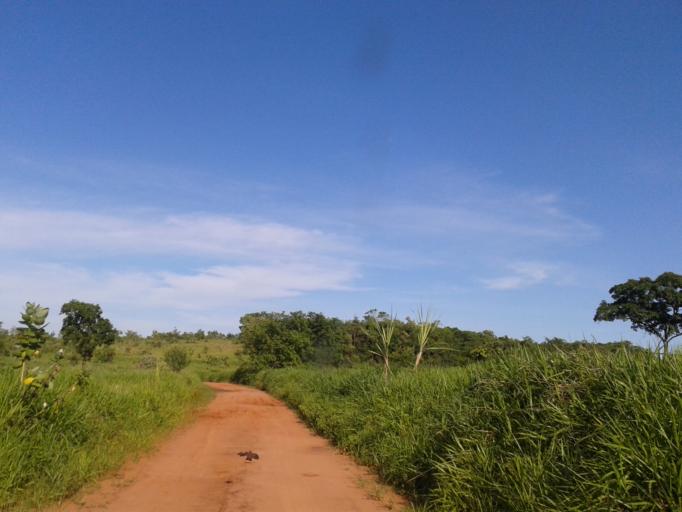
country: BR
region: Minas Gerais
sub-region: Santa Vitoria
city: Santa Vitoria
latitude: -19.1204
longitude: -50.0005
